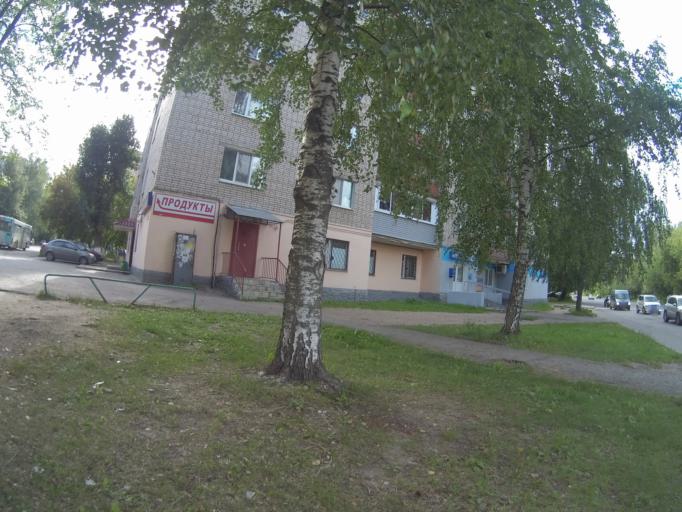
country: RU
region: Vladimir
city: Vladimir
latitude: 56.1503
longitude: 40.4299
